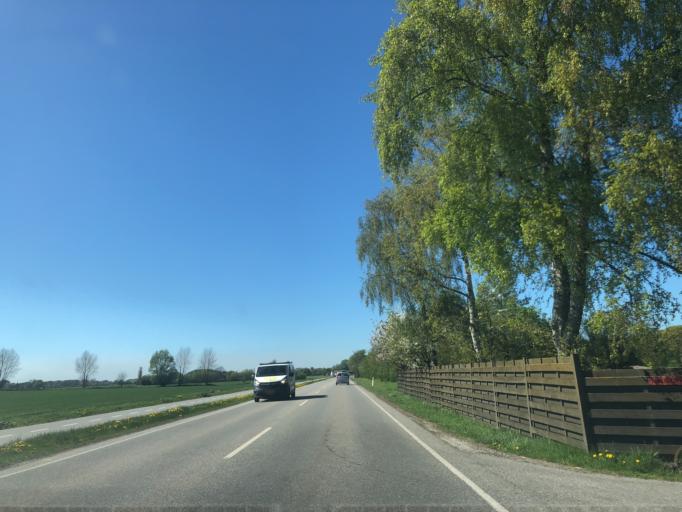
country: DK
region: Zealand
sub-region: Stevns Kommune
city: Store Heddinge
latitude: 55.3378
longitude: 12.3473
